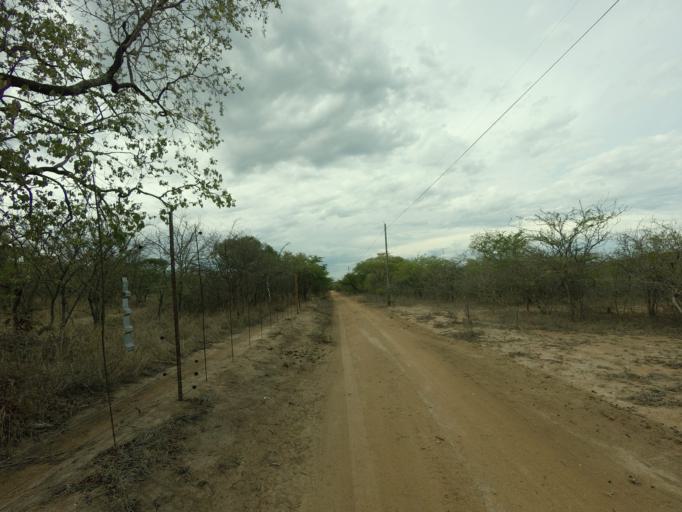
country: ZA
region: Limpopo
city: Thulamahashi
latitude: -24.5250
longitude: 31.1102
